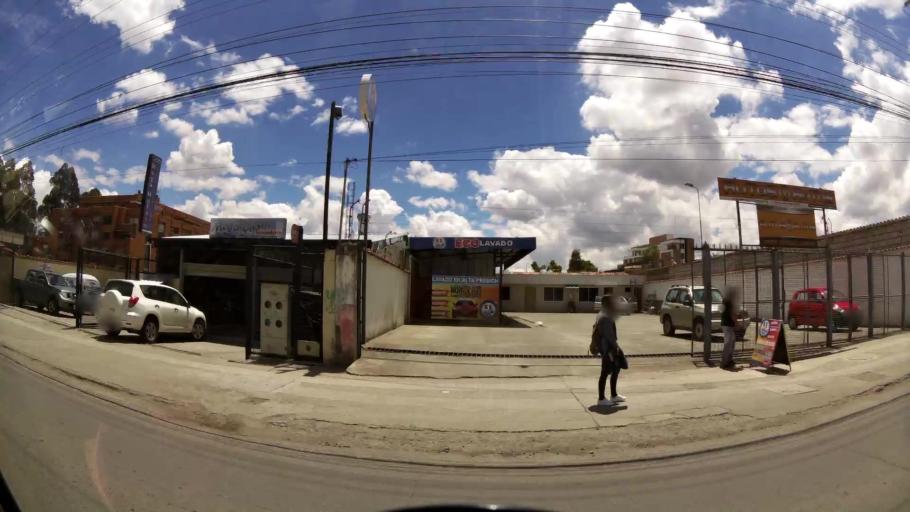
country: EC
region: Azuay
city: Cuenca
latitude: -2.9084
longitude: -79.0342
